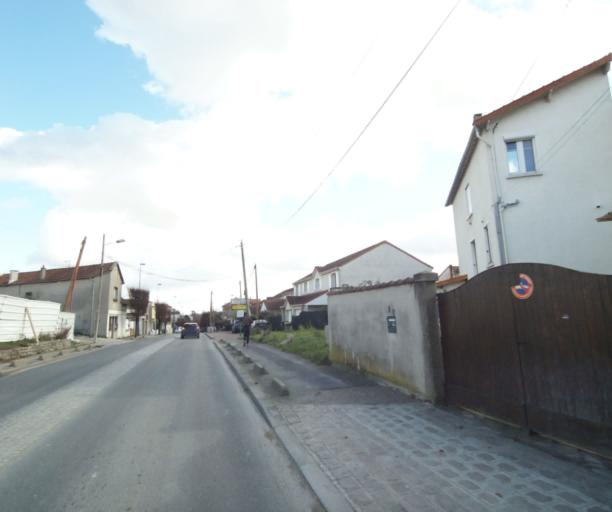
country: FR
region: Ile-de-France
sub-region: Departement de Seine-Saint-Denis
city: Pierrefitte-sur-Seine
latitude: 48.9637
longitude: 2.3529
